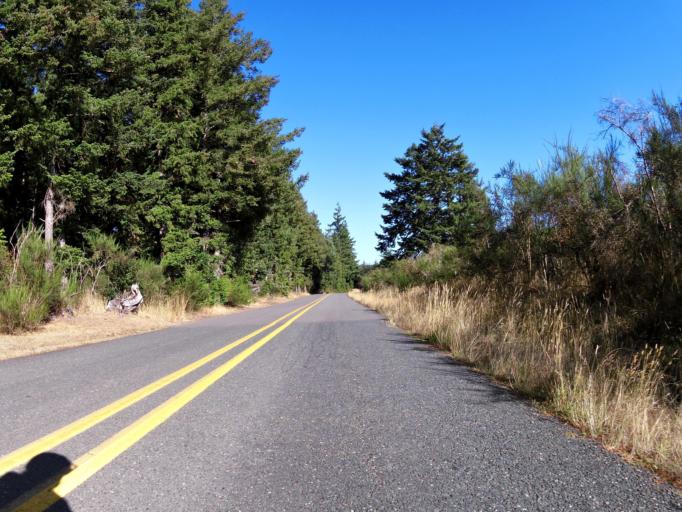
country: US
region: Oregon
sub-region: Coos County
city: Bandon
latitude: 43.0396
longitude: -124.4093
